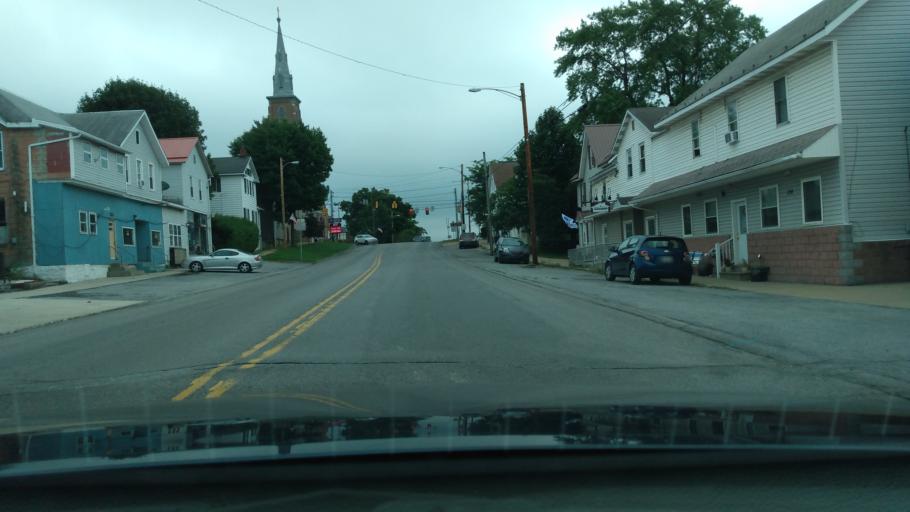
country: US
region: Pennsylvania
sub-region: Cambria County
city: Hastings
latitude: 40.6040
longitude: -78.7090
